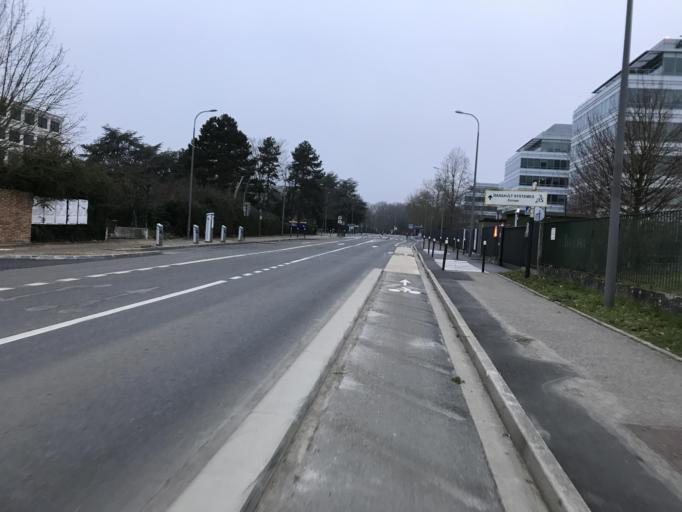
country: FR
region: Ile-de-France
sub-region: Departement des Yvelines
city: Velizy-Villacoublay
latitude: 48.7854
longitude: 2.2124
